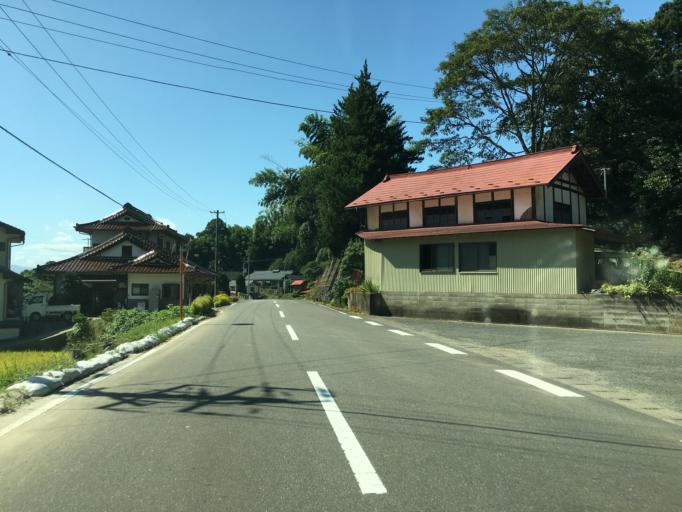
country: JP
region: Fukushima
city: Sukagawa
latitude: 37.2806
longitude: 140.4563
